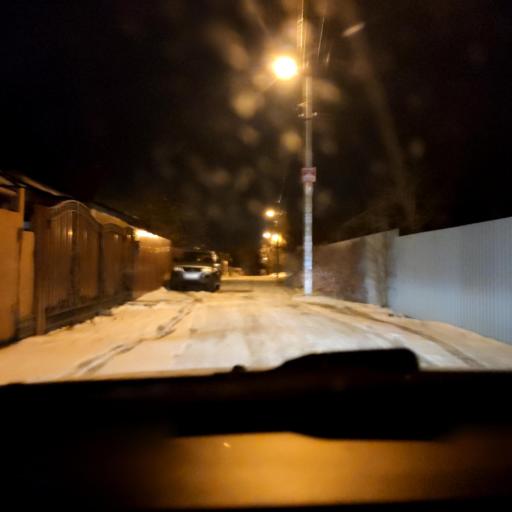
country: RU
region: Voronezj
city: Pridonskoy
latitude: 51.6852
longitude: 39.0687
